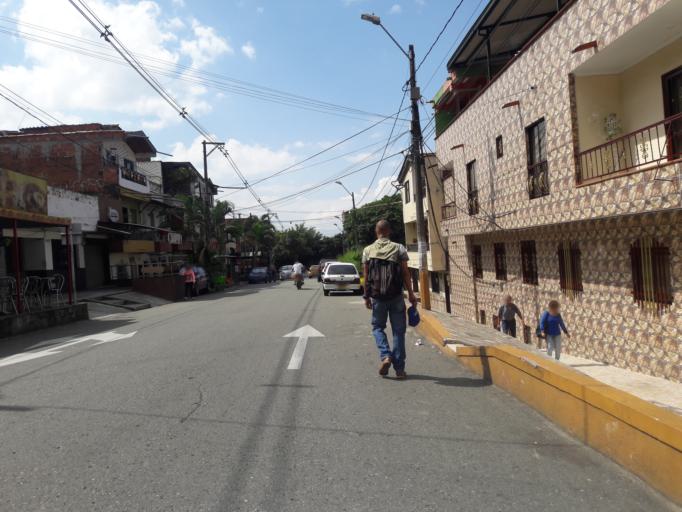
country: CO
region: Antioquia
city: Medellin
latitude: 6.2571
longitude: -75.5515
